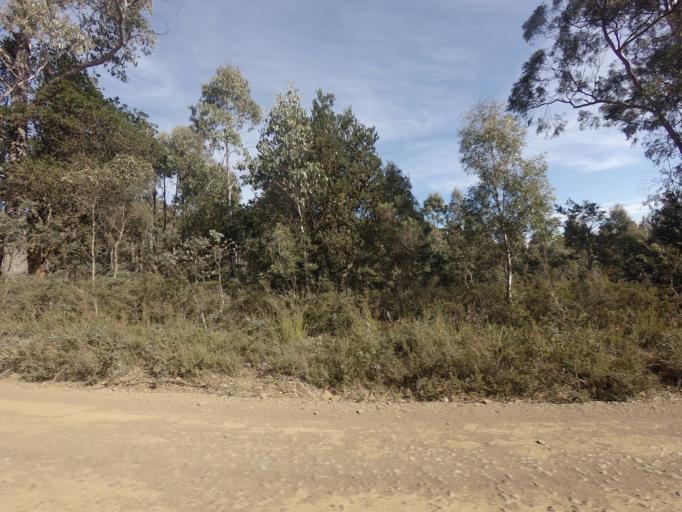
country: AU
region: Tasmania
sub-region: Sorell
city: Sorell
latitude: -42.4984
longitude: 147.5315
